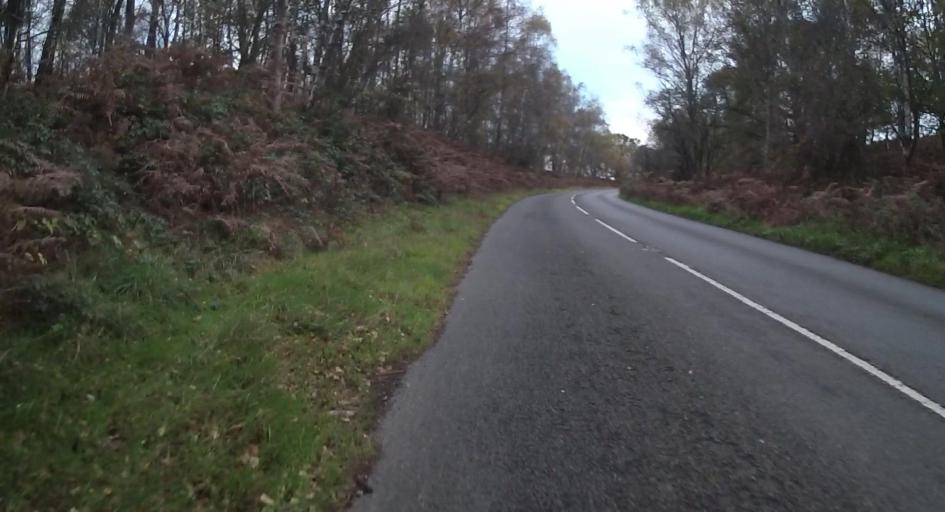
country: GB
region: England
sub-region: Hampshire
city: Lindford
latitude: 51.1281
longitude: -0.8519
